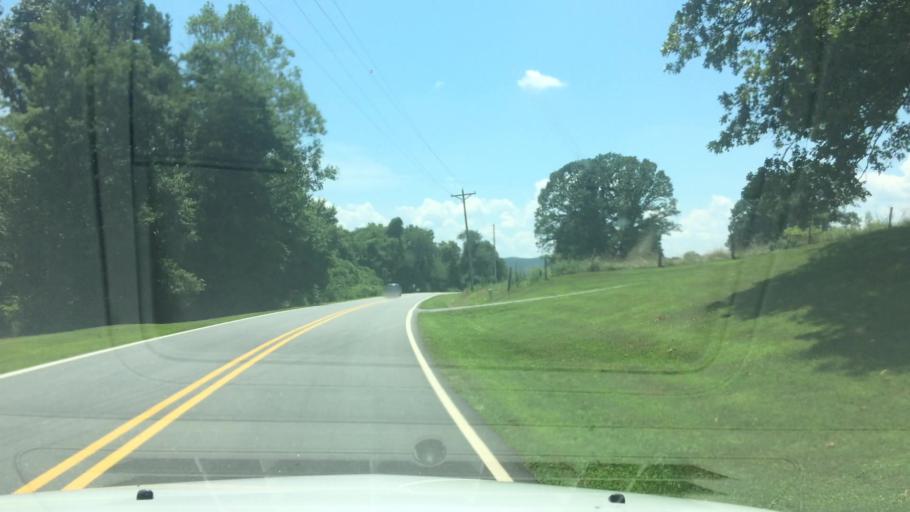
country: US
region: North Carolina
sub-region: Alexander County
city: Taylorsville
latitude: 35.9517
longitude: -81.2673
